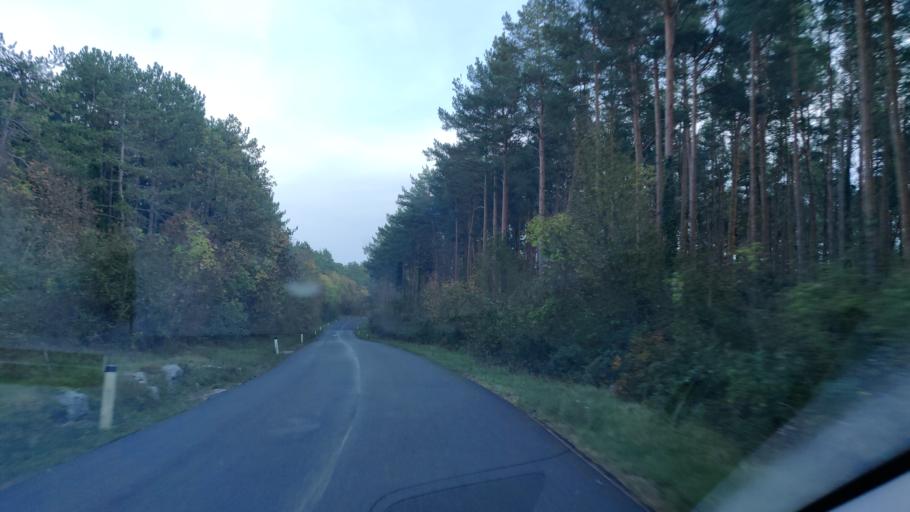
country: SI
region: Sezana
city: Sezana
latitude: 45.7734
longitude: 13.8747
